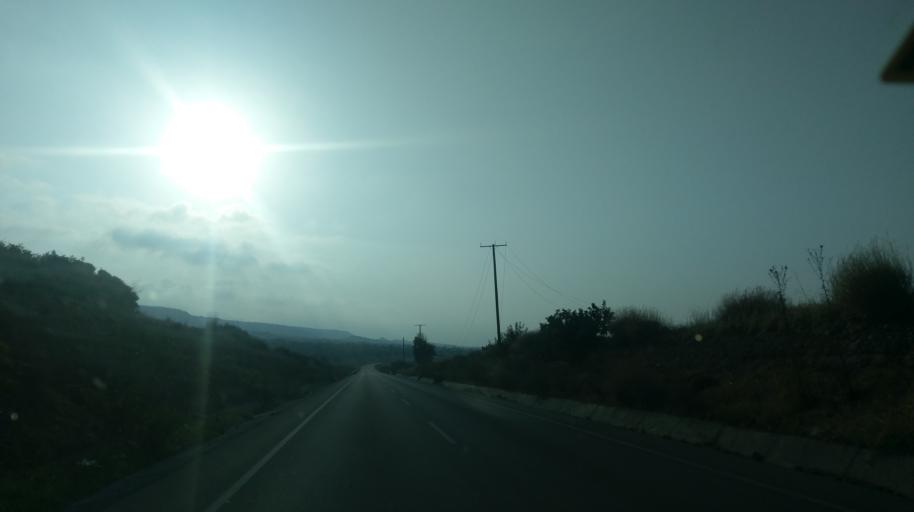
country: CY
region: Ammochostos
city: Trikomo
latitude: 35.4328
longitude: 33.9374
